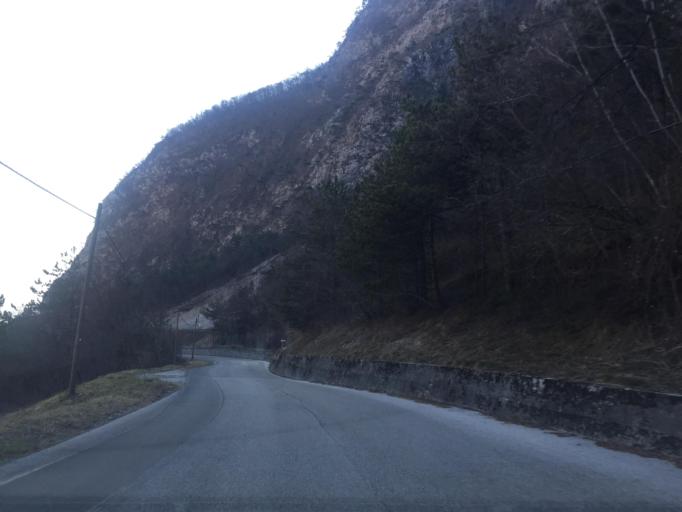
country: IT
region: Friuli Venezia Giulia
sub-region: Provincia di Udine
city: Tolmezzo
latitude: 46.4110
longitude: 13.0428
